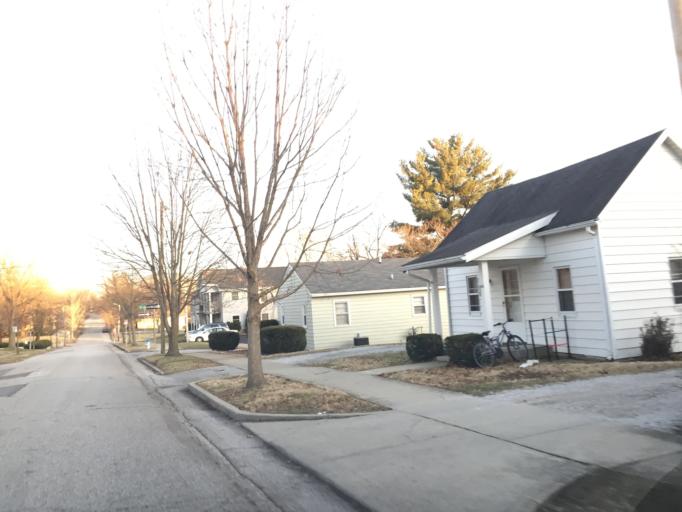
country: US
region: Indiana
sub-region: Monroe County
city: Bloomington
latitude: 39.1744
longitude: -86.5288
